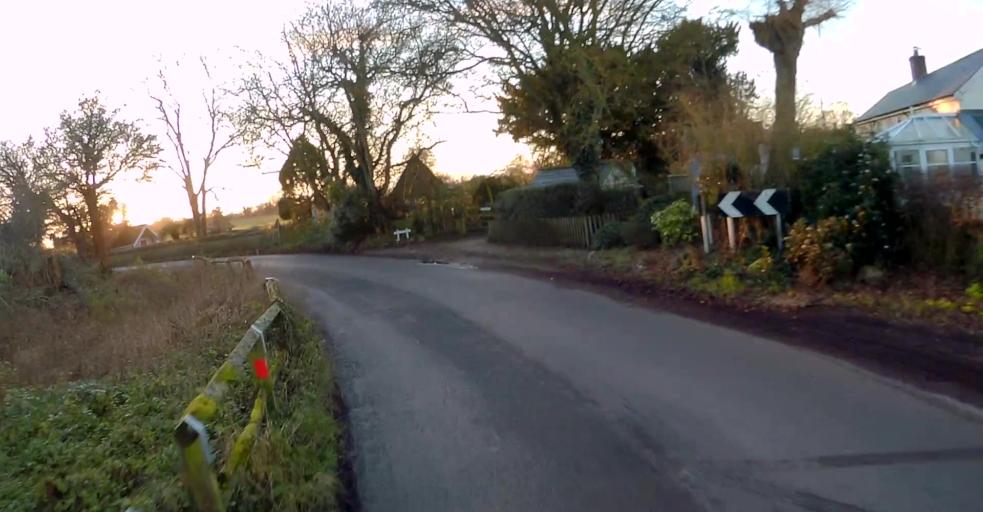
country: GB
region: England
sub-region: West Berkshire
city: Stratfield Mortimer
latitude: 51.3490
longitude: -1.0273
